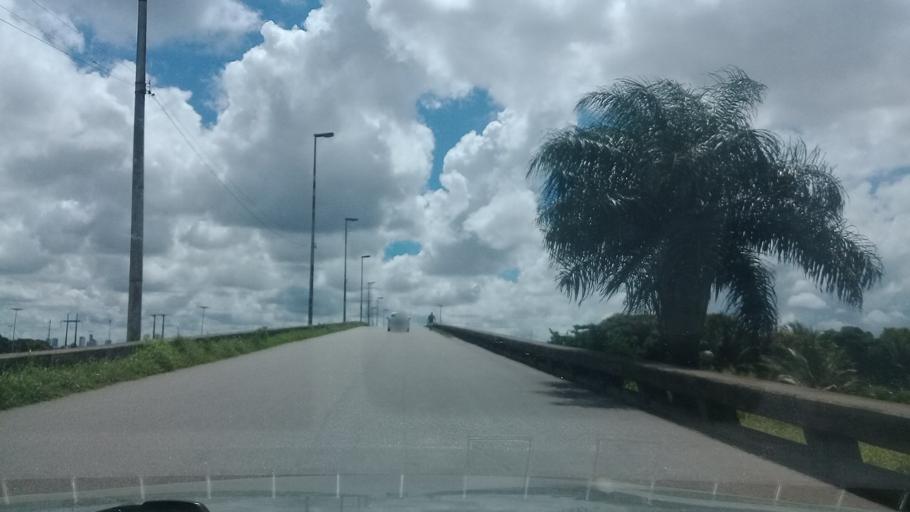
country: BR
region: Pernambuco
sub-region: Recife
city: Recife
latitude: -8.0696
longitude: -34.9416
